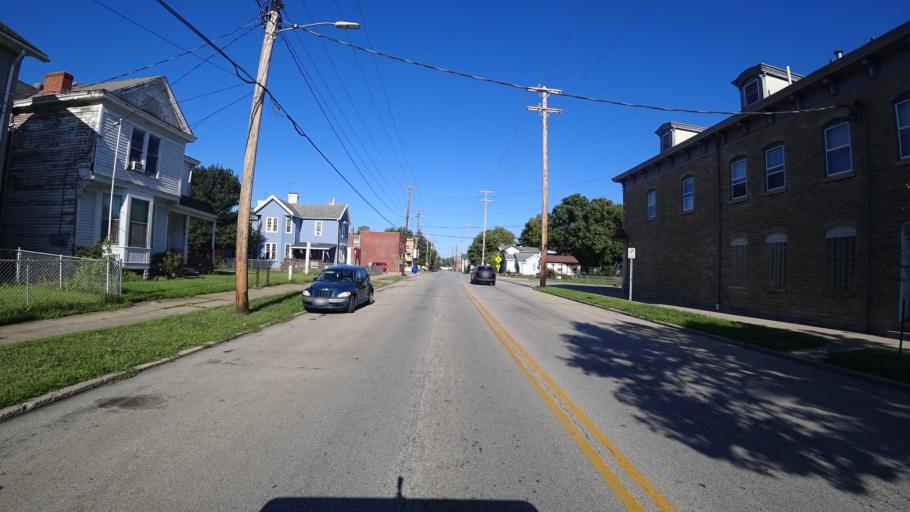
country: US
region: Ohio
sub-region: Butler County
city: Hamilton
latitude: 39.4020
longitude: -84.5512
